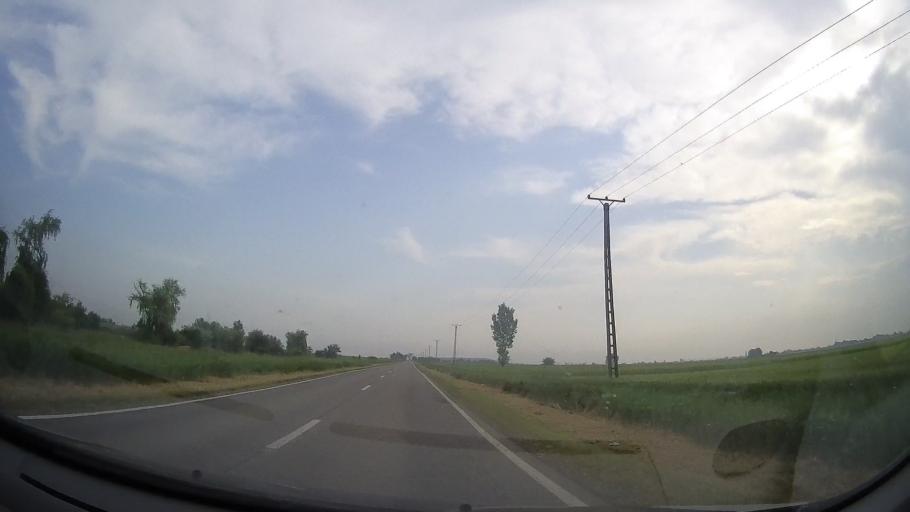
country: RO
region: Timis
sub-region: Comuna Sag
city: Sag
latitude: 45.6641
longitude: 21.1521
